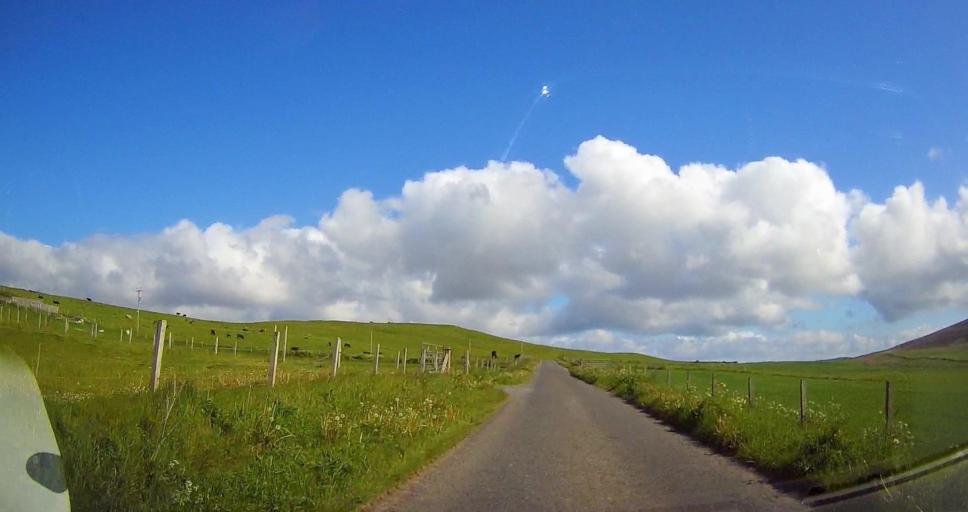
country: GB
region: Scotland
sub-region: Orkney Islands
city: Stromness
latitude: 58.9822
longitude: -3.1397
